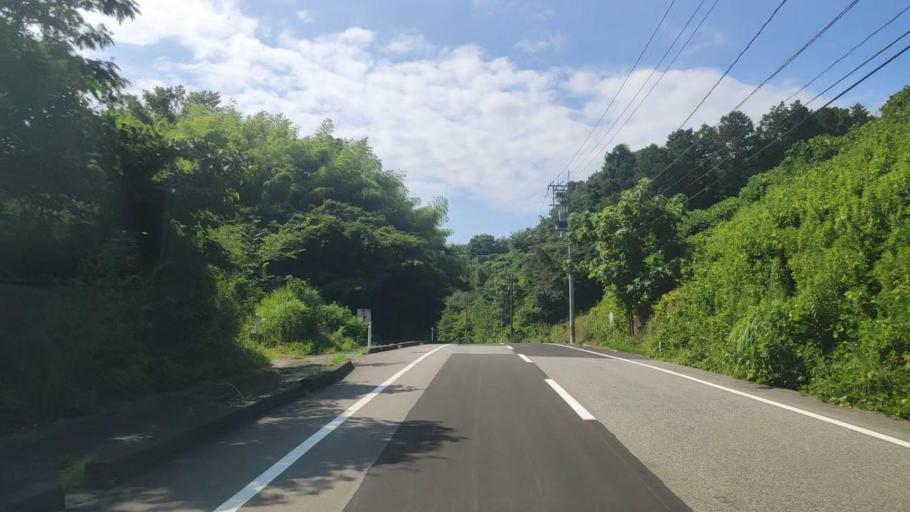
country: JP
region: Ishikawa
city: Komatsu
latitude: 36.3848
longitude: 136.4961
